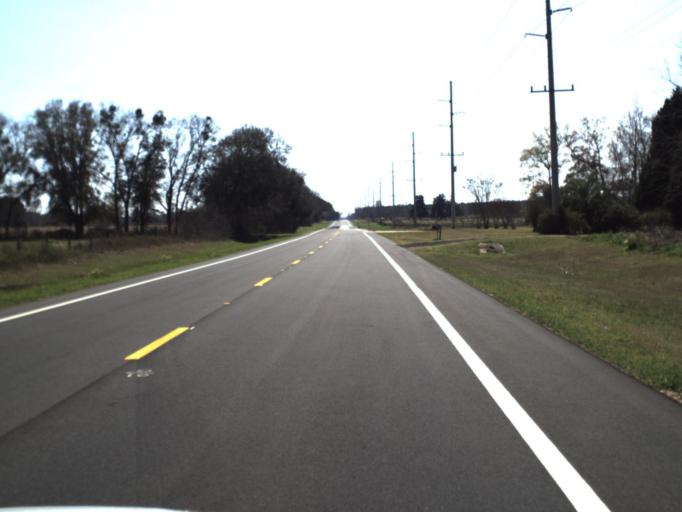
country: US
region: Florida
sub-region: Jackson County
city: Sneads
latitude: 30.7755
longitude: -85.0191
